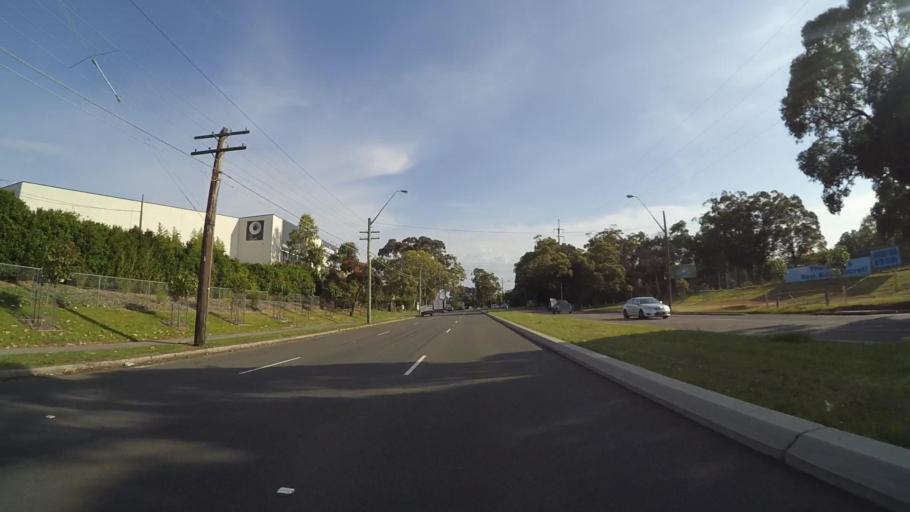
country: AU
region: New South Wales
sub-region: Sutherland Shire
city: Miranda
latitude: -34.0262
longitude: 151.1064
